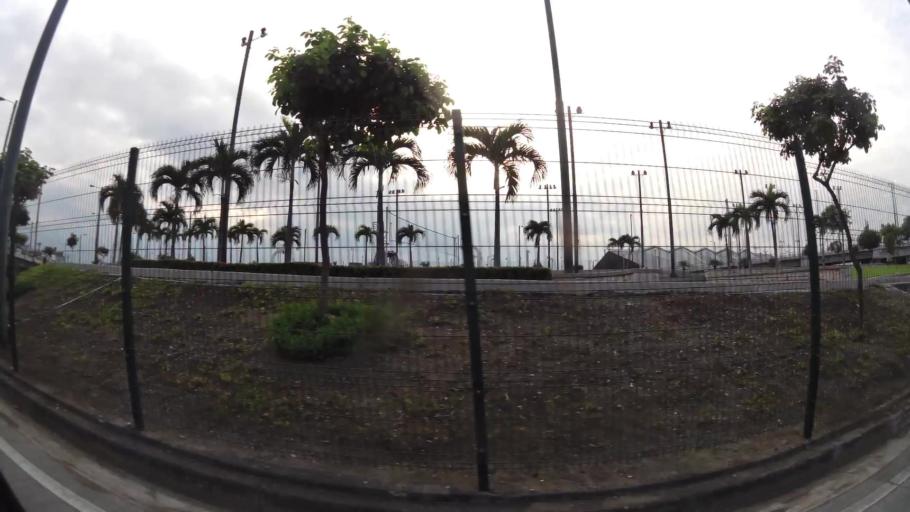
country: EC
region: Guayas
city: Eloy Alfaro
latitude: -2.1391
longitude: -79.8831
